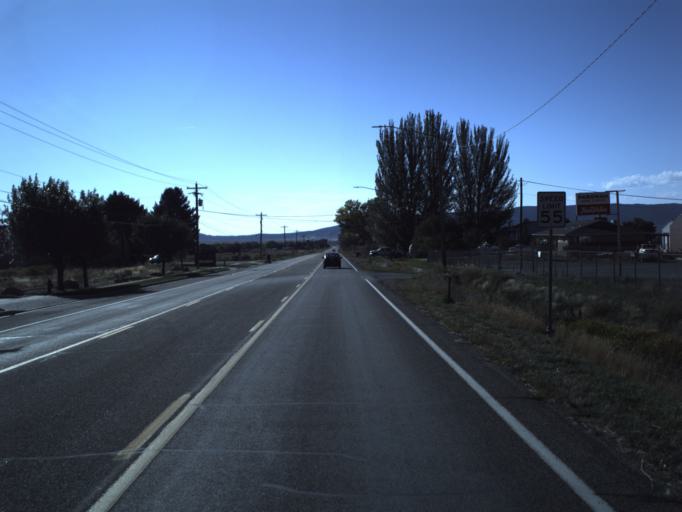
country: US
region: Utah
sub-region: Iron County
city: Parowan
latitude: 37.8387
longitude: -112.8439
